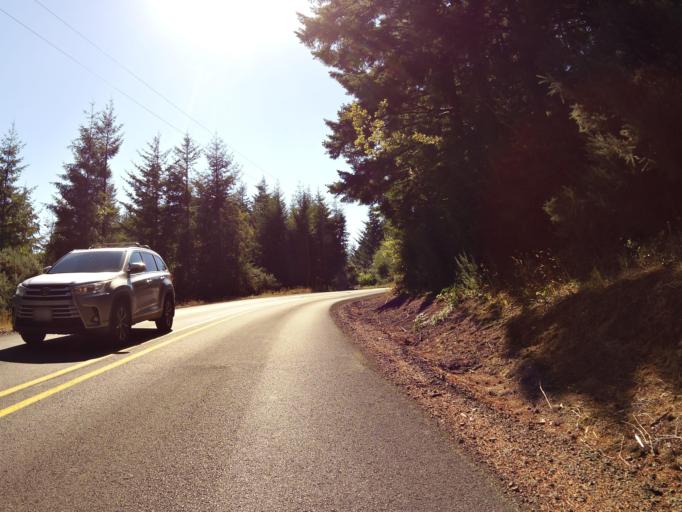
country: US
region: Oregon
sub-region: Coos County
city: Bandon
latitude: 43.2147
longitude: -124.3638
